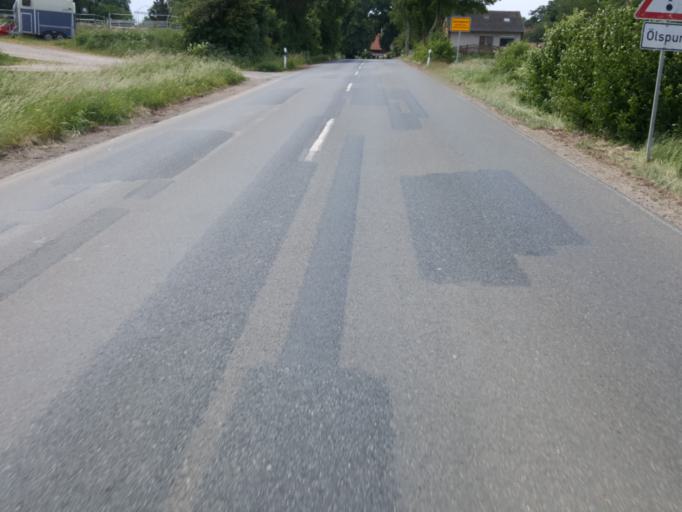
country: DE
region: Lower Saxony
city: Husum
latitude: 52.5990
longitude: 9.2462
